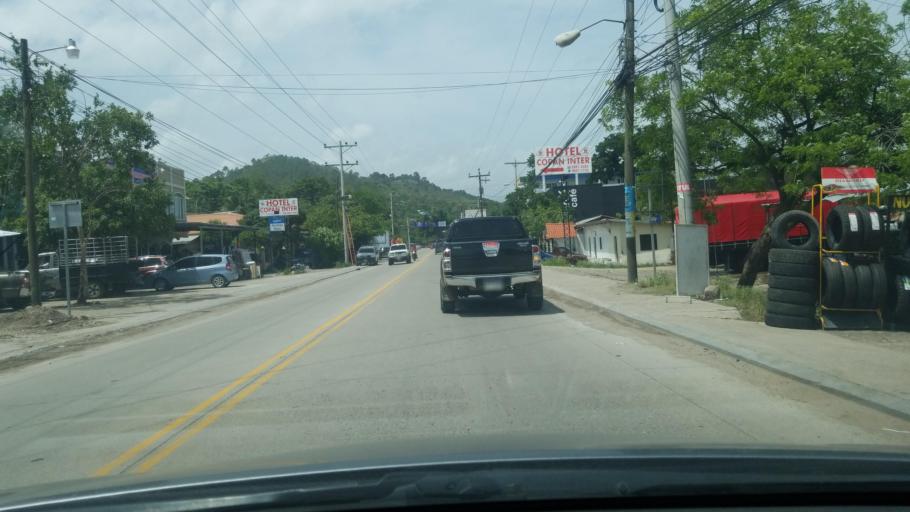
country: HN
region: Copan
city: La Entrada
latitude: 15.0554
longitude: -88.7552
